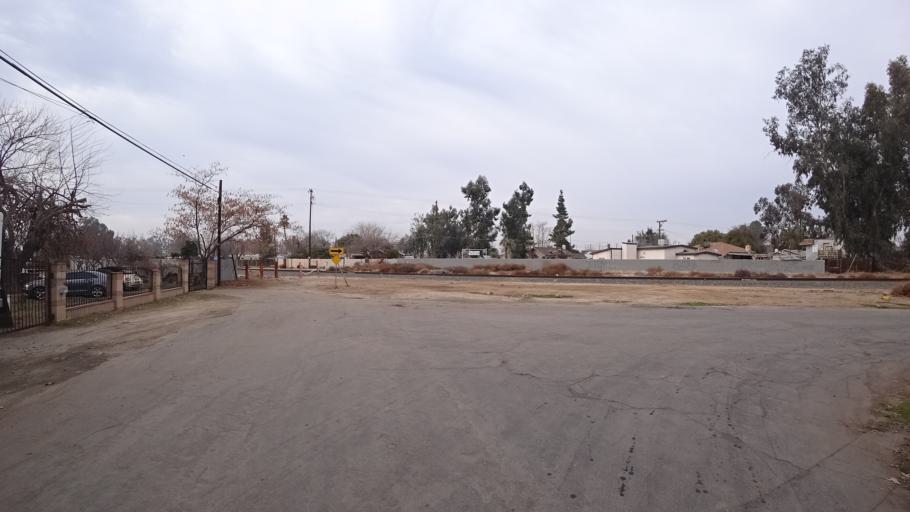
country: US
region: California
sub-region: Kern County
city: Bakersfield
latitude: 35.3421
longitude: -118.9993
